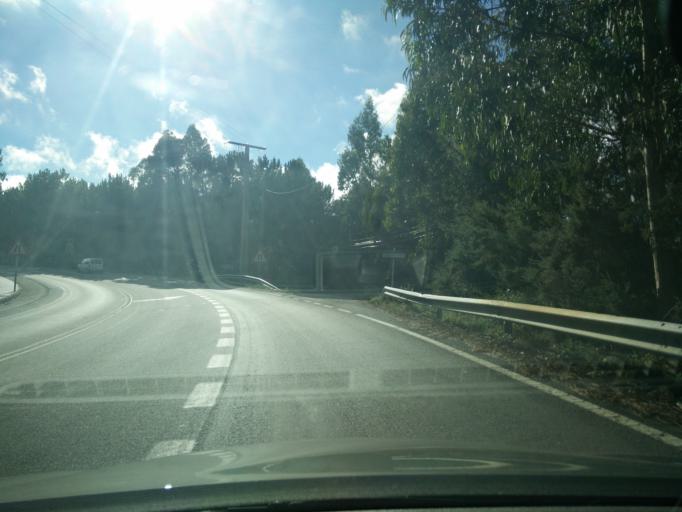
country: ES
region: Galicia
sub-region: Provincia da Coruna
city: Laxe
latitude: 43.2335
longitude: -8.9087
